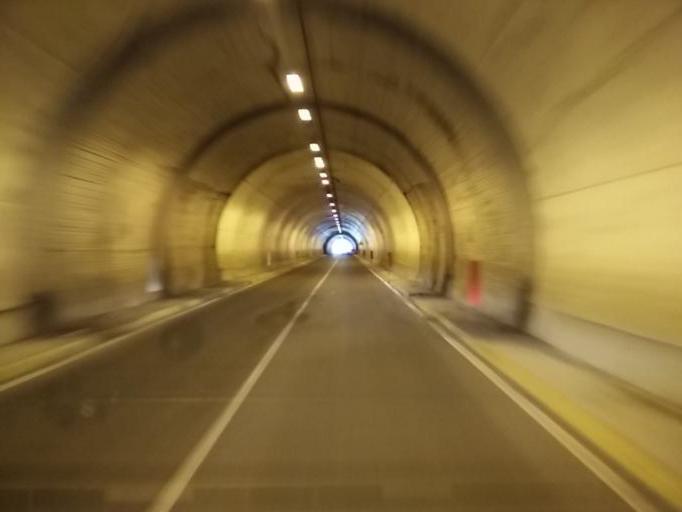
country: IT
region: Lombardy
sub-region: Provincia di Brescia
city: Anfo
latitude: 45.7433
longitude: 10.4992
